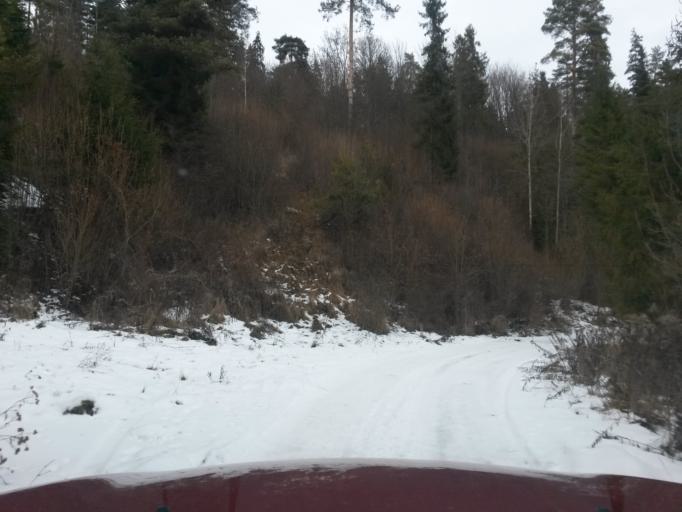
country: SK
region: Kosicky
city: Spisska Nova Ves
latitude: 48.8904
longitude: 20.6065
